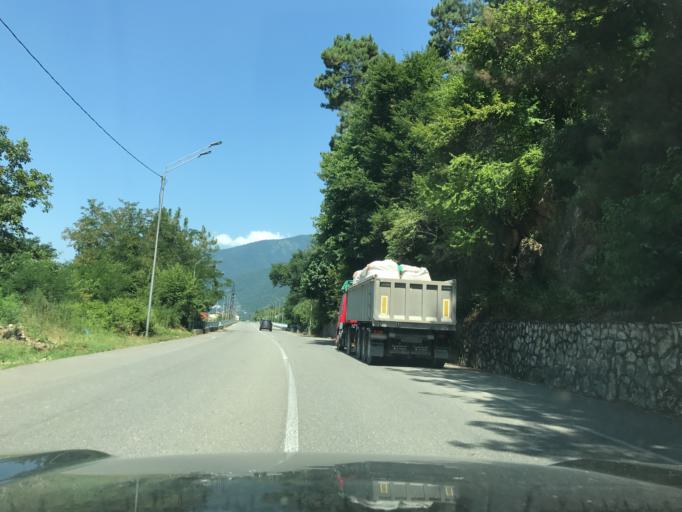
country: GE
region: Abkhazia
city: Gagra
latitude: 43.2912
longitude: 40.2683
